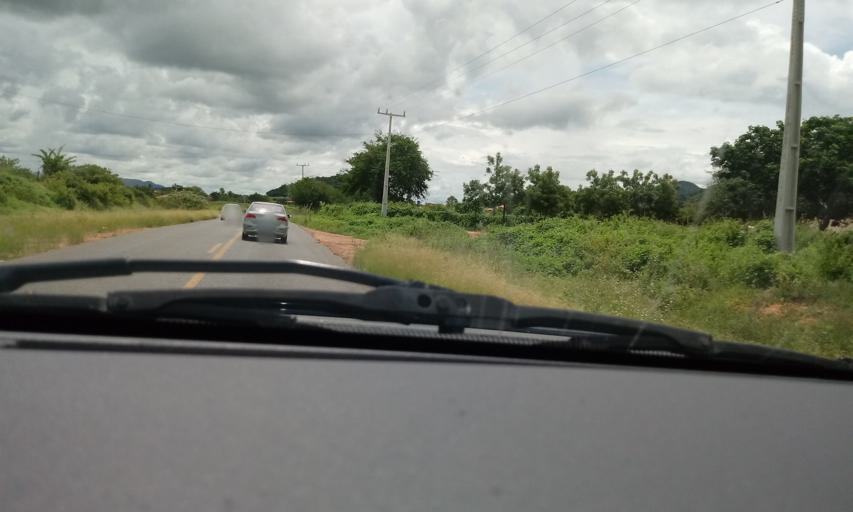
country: BR
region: Bahia
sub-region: Guanambi
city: Guanambi
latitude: -14.1205
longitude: -42.8552
